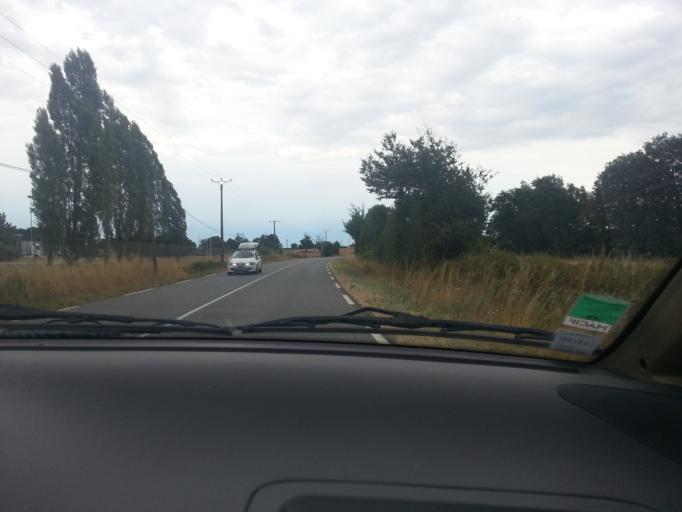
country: FR
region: Auvergne
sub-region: Departement de l'Allier
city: Saint-Gerand-le-Puy
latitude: 46.2098
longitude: 3.5069
